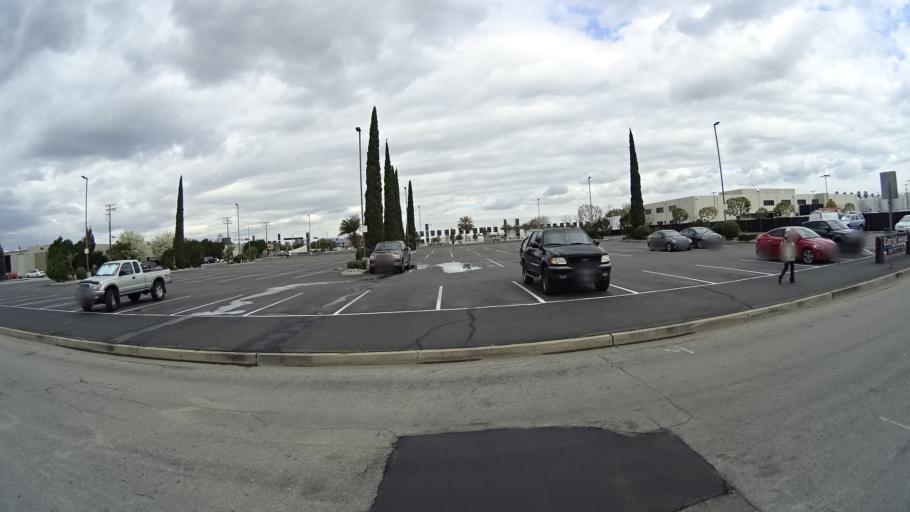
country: US
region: California
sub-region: Orange County
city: Placentia
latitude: 33.8506
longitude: -117.8518
